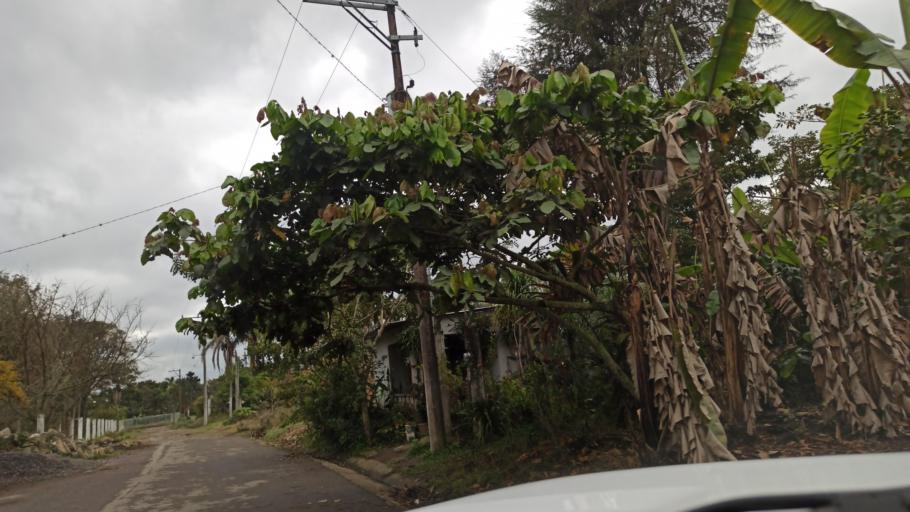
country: MX
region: Veracruz
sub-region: Chocaman
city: San Jose Neria
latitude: 18.9930
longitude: -96.9988
